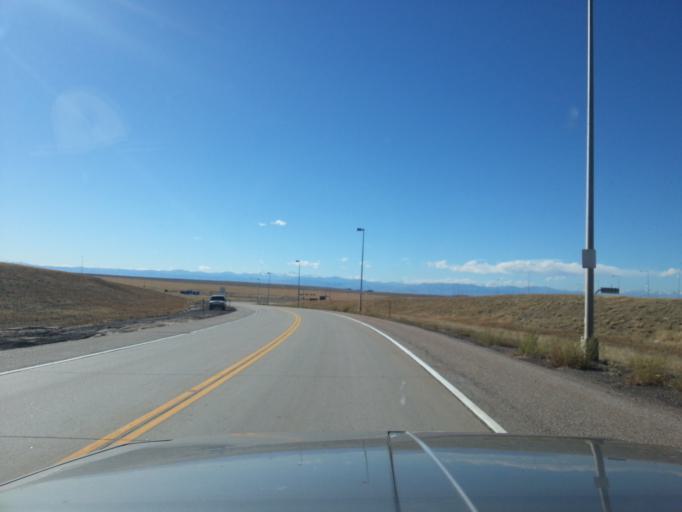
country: US
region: Colorado
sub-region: Adams County
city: Aurora
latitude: 39.8331
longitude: -104.7106
